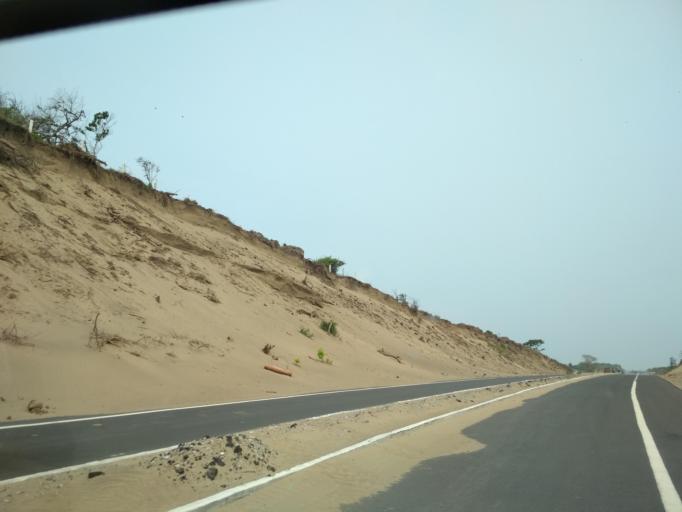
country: MX
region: Veracruz
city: Anton Lizardo
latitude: 19.0432
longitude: -95.9940
